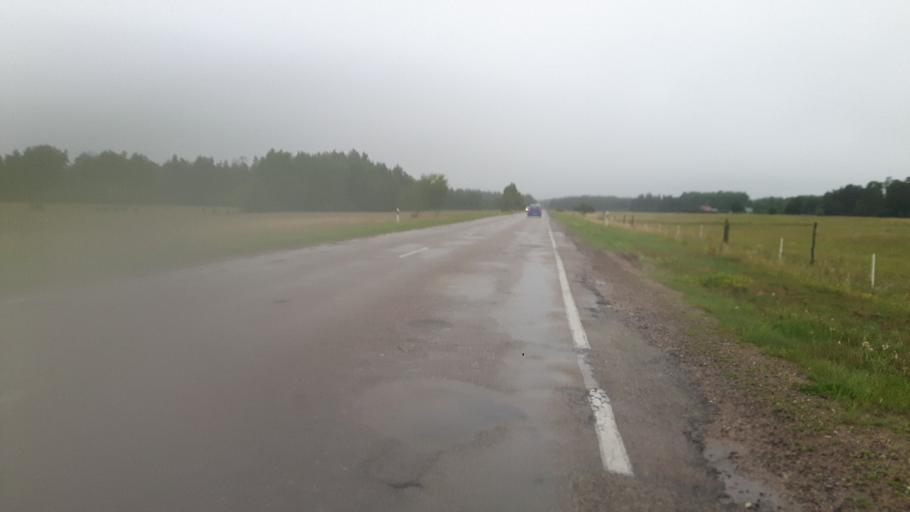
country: LV
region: Rucavas
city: Rucava
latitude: 56.0965
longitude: 21.1306
